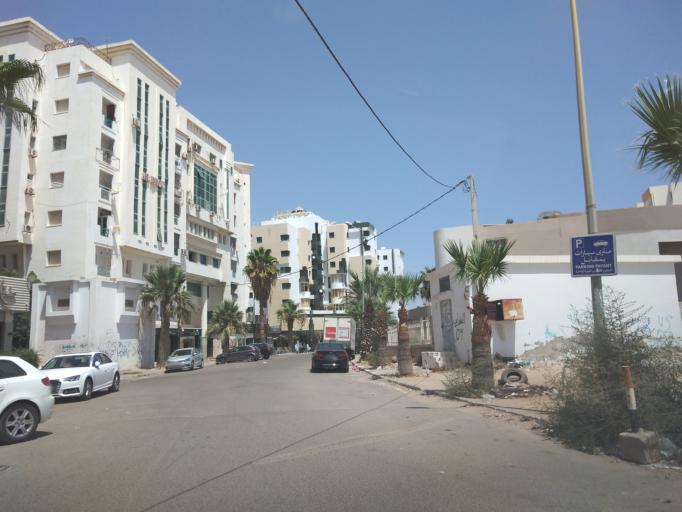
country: TN
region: Safaqis
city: Sfax
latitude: 34.7365
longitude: 10.7500
